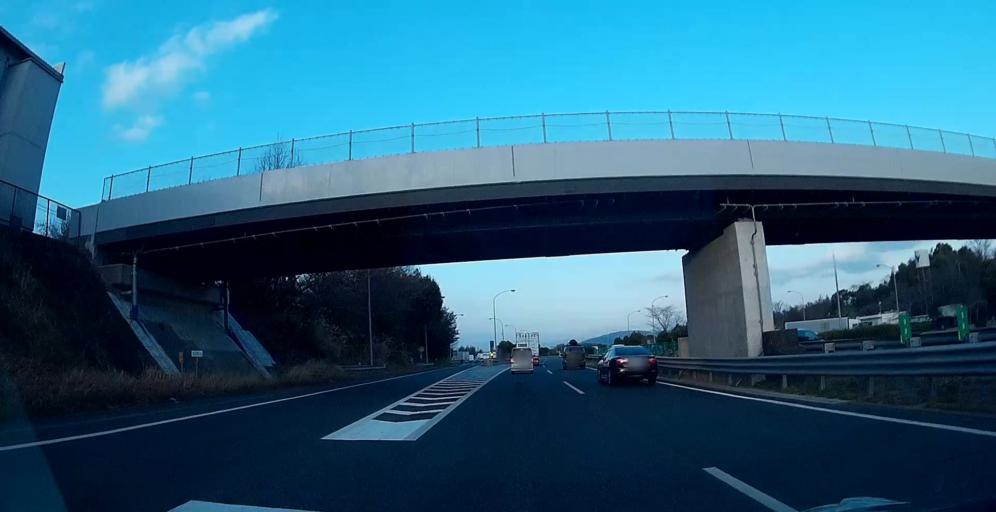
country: JP
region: Kumamoto
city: Uto
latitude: 32.7075
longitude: 130.7555
